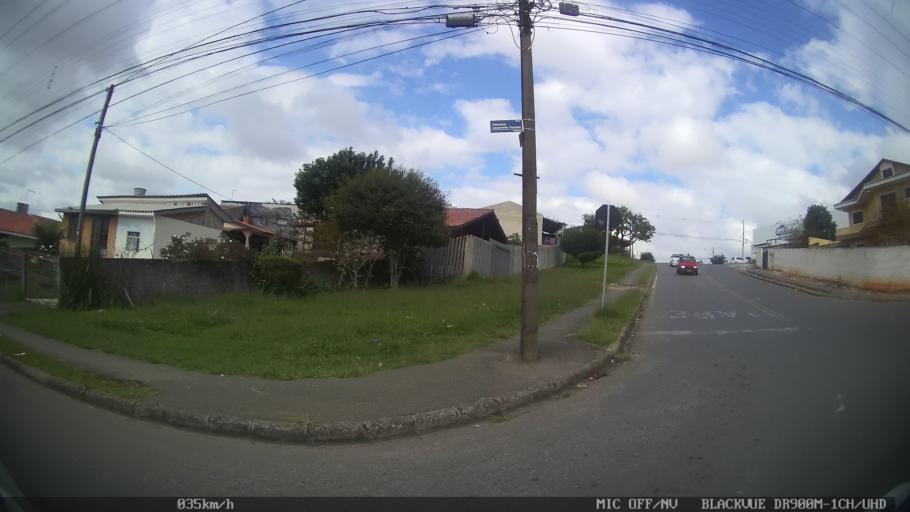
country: BR
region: Parana
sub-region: Colombo
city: Colombo
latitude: -25.3594
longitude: -49.1910
